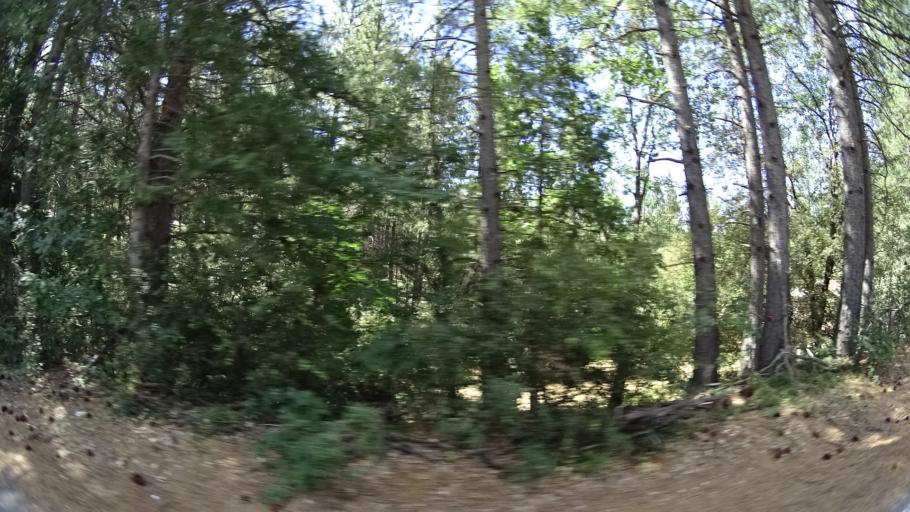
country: US
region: California
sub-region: Amador County
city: Pioneer
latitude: 38.3391
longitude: -120.5494
